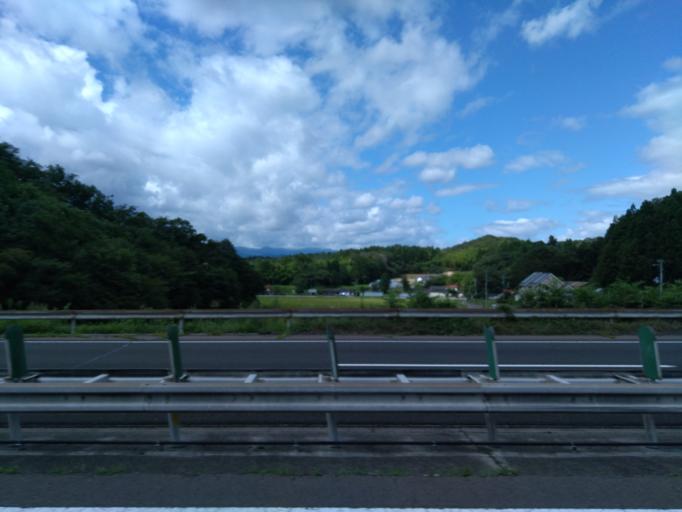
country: JP
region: Miyagi
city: Tomiya
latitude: 38.4575
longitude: 140.9076
